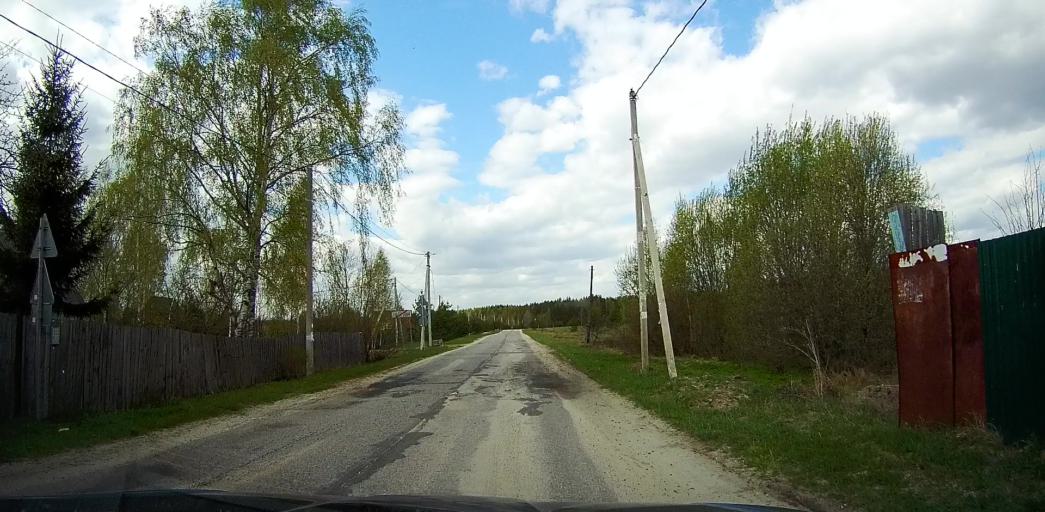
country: RU
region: Moskovskaya
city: Davydovo
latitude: 55.6398
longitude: 38.7771
